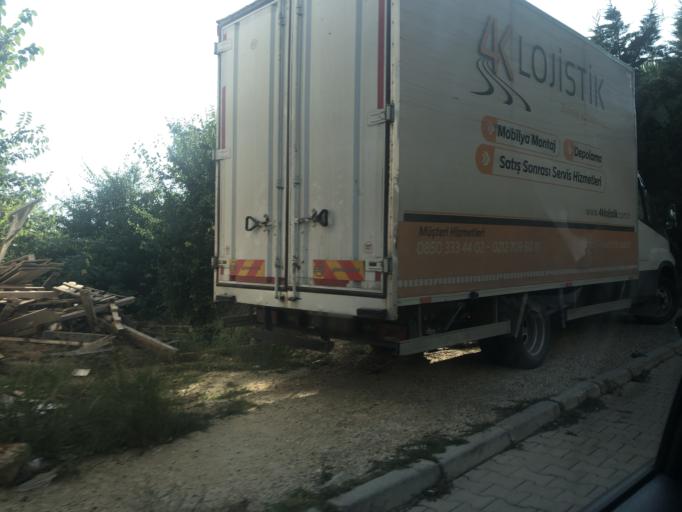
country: TR
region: Istanbul
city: Catalca
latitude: 41.2237
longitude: 28.4768
